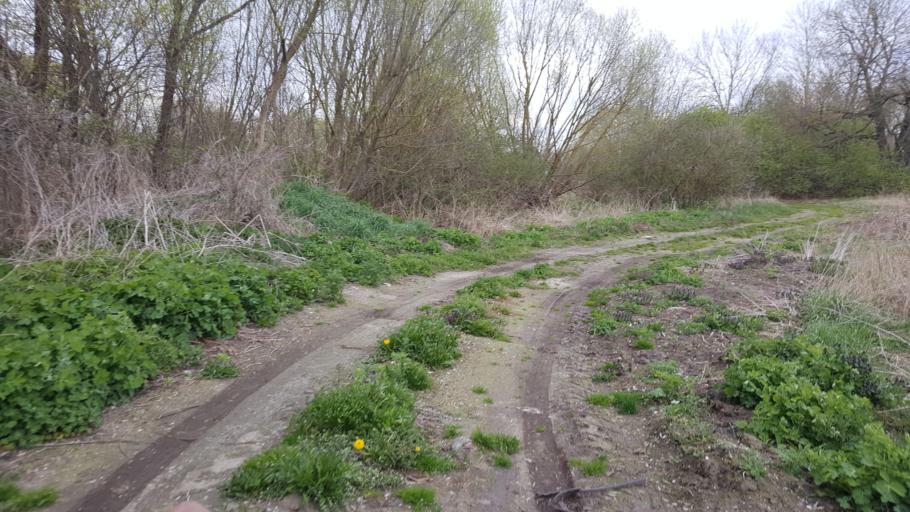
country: BY
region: Brest
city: Kamyanyets
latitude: 52.4072
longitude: 23.7080
